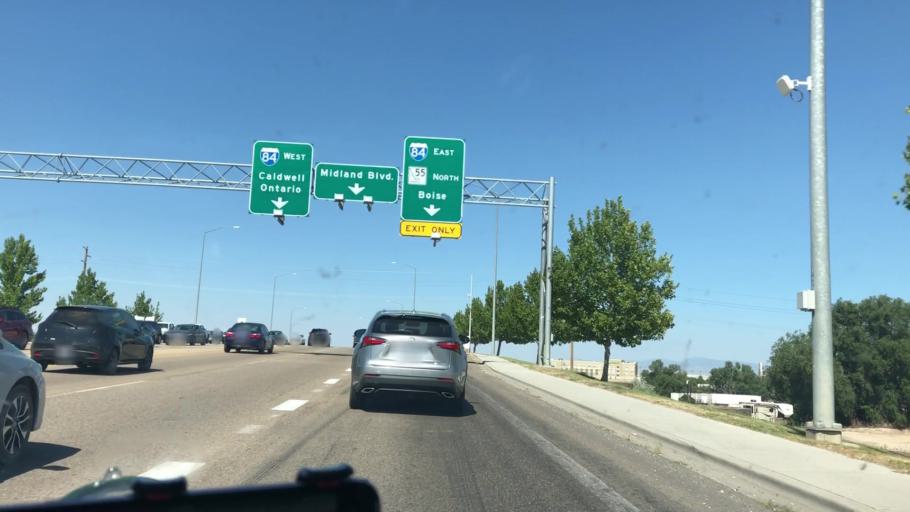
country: US
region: Idaho
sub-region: Canyon County
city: Nampa
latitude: 43.6065
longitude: -116.6010
